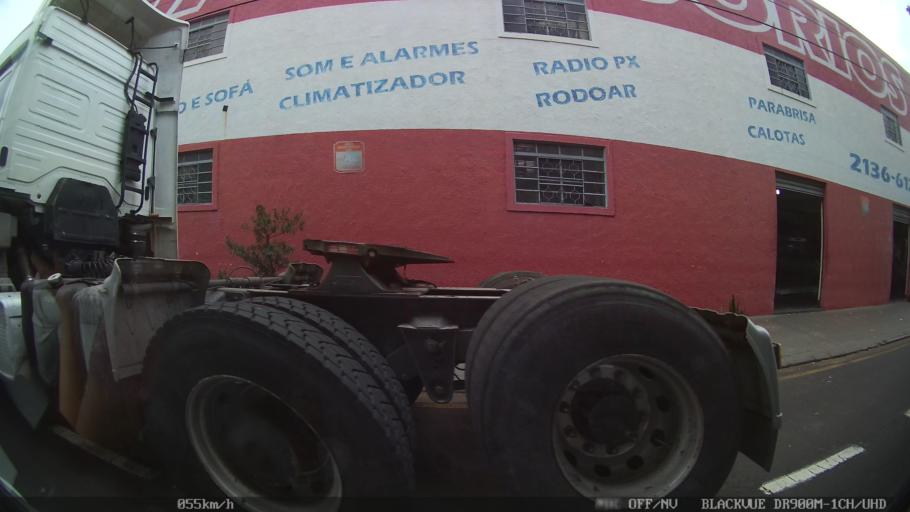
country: BR
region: Sao Paulo
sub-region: Sao Jose Do Rio Preto
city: Sao Jose do Rio Preto
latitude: -20.8233
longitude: -49.3727
